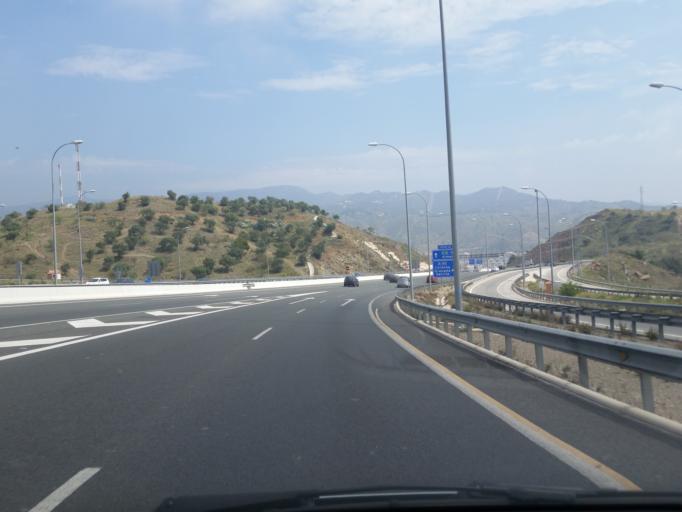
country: ES
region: Andalusia
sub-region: Provincia de Malaga
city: Malaga
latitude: 36.7463
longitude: -4.4409
